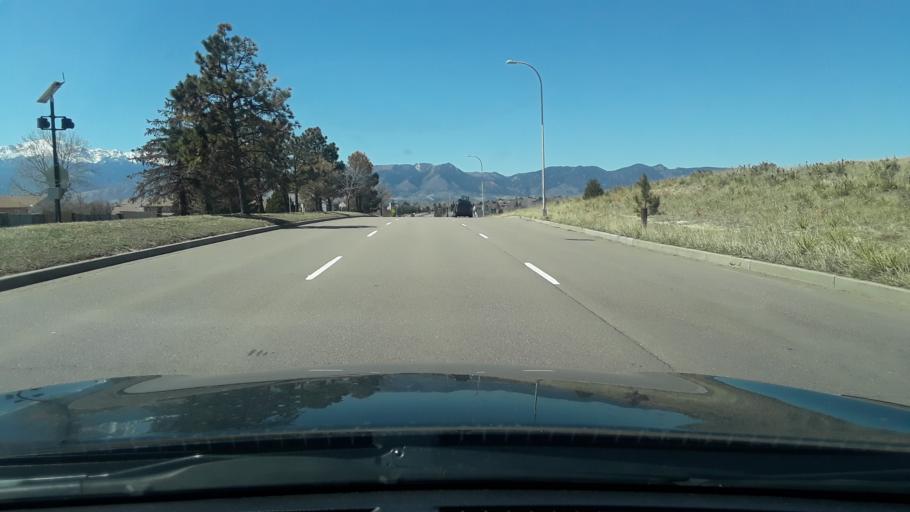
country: US
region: Colorado
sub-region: El Paso County
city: Black Forest
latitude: 38.9547
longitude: -104.7348
